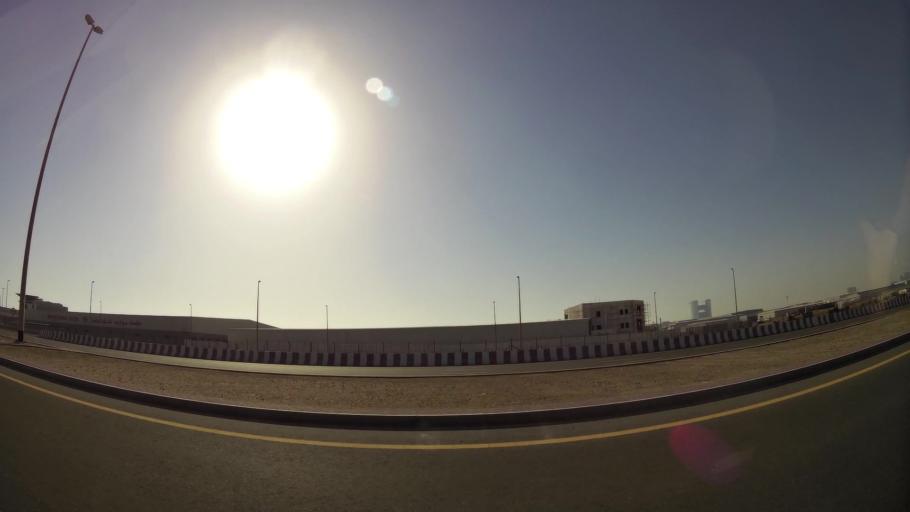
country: AE
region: Dubai
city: Dubai
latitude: 24.9459
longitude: 55.0890
